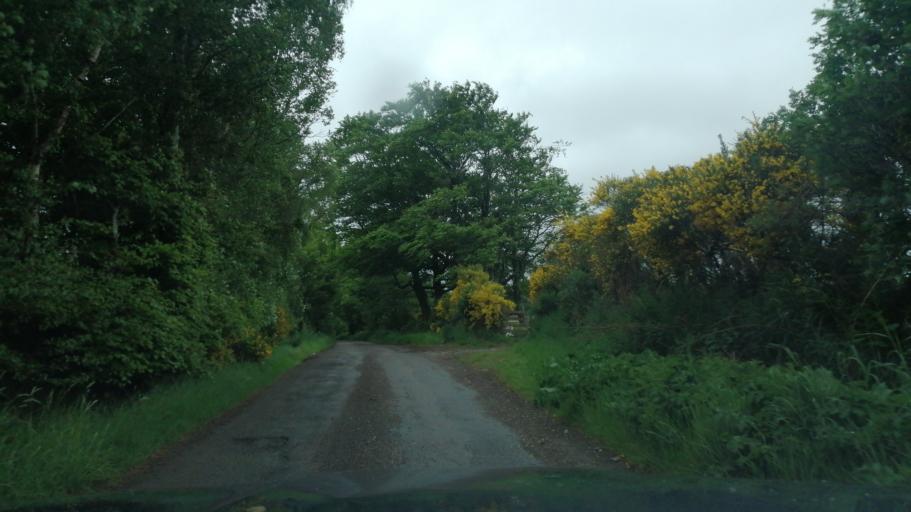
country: GB
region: Scotland
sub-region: Moray
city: Keith
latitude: 57.5642
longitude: -2.8617
